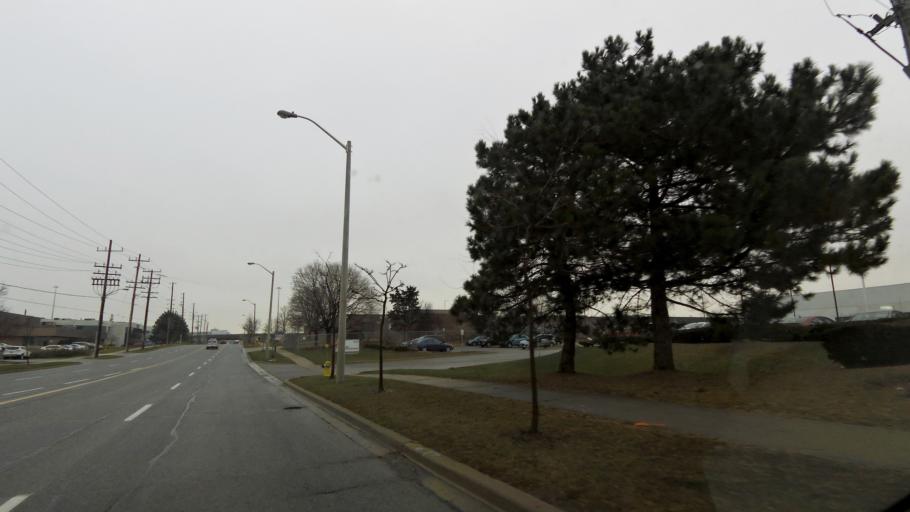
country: CA
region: Ontario
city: Etobicoke
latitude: 43.6940
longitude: -79.5988
